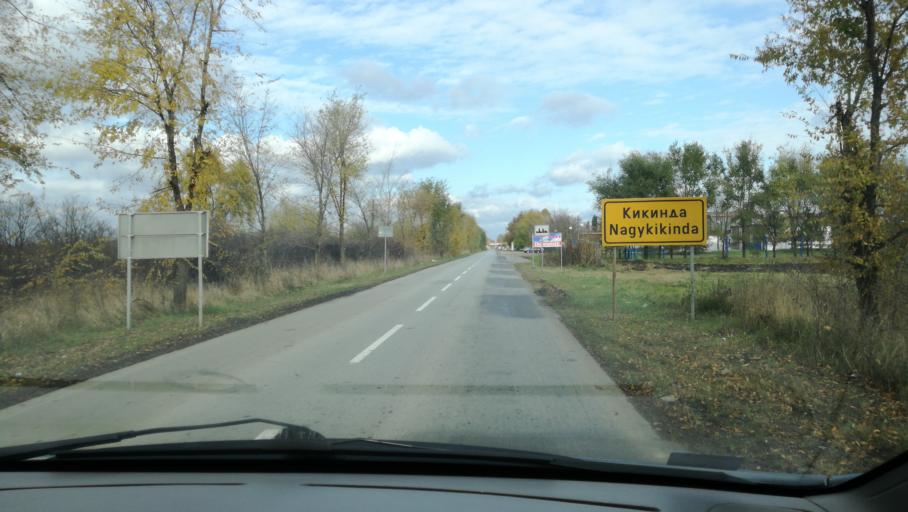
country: RS
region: Autonomna Pokrajina Vojvodina
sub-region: Severnobanatski Okrug
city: Kikinda
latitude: 45.8008
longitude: 20.4415
